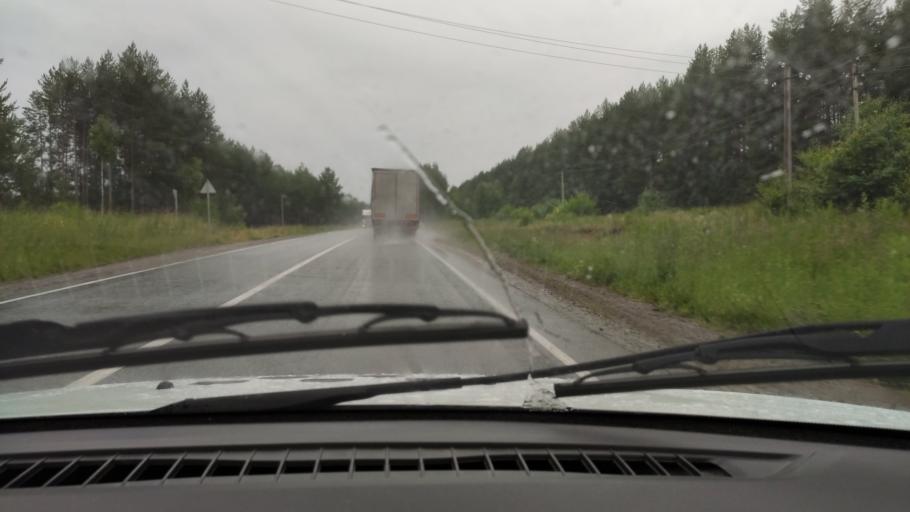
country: RU
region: Udmurtiya
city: Votkinsk
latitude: 57.1221
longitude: 54.1077
